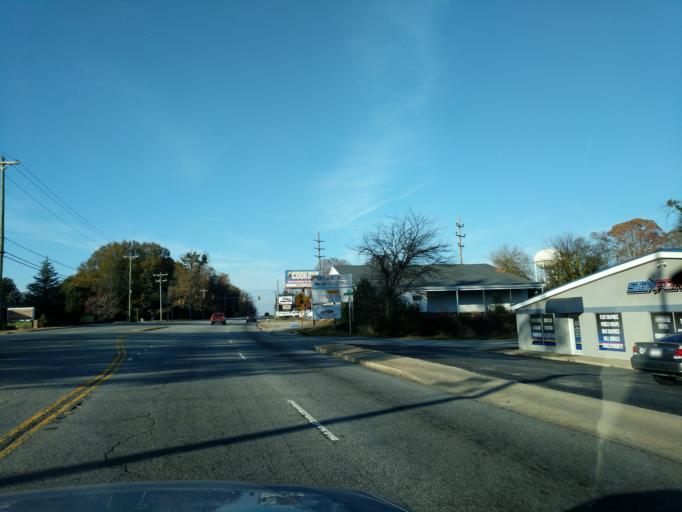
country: US
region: South Carolina
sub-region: Spartanburg County
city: Saxon
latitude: 34.9836
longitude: -81.9456
